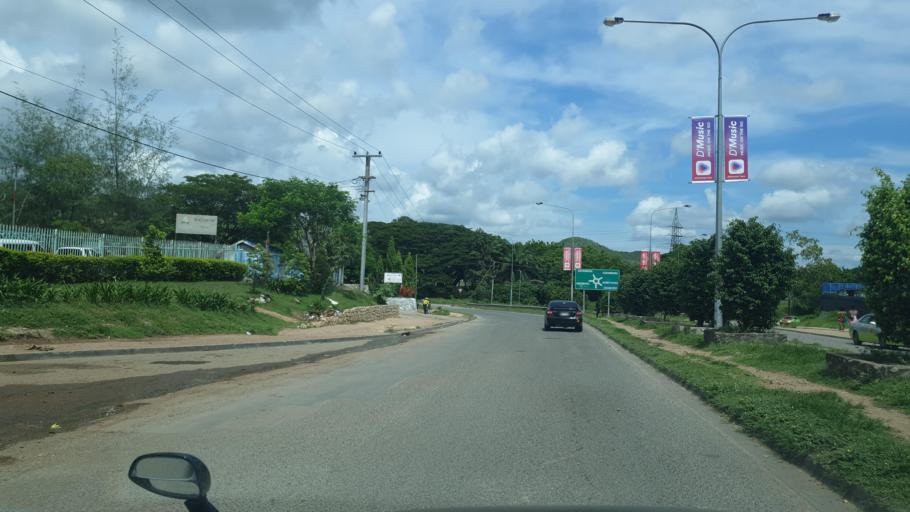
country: PG
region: National Capital
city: Port Moresby
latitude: -9.3994
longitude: 147.1604
